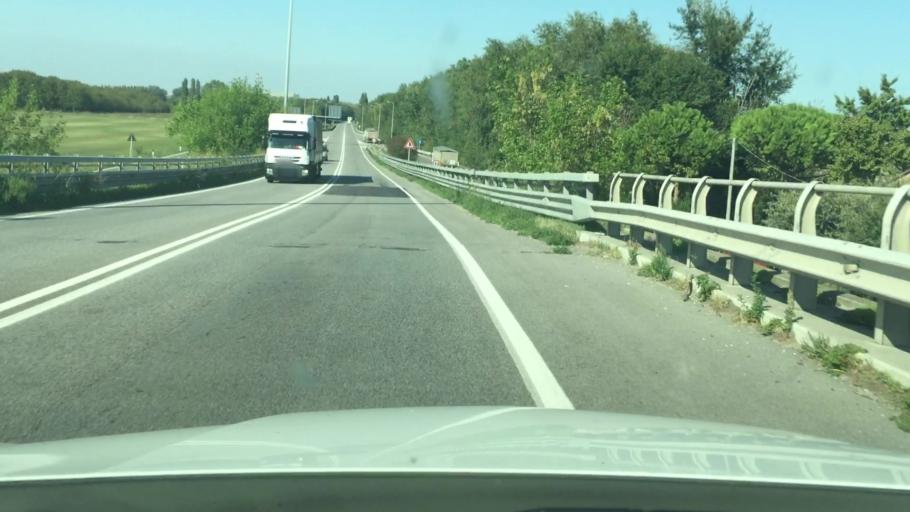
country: IT
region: Emilia-Romagna
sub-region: Provincia di Ravenna
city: Ravenna
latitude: 44.4590
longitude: 12.2089
